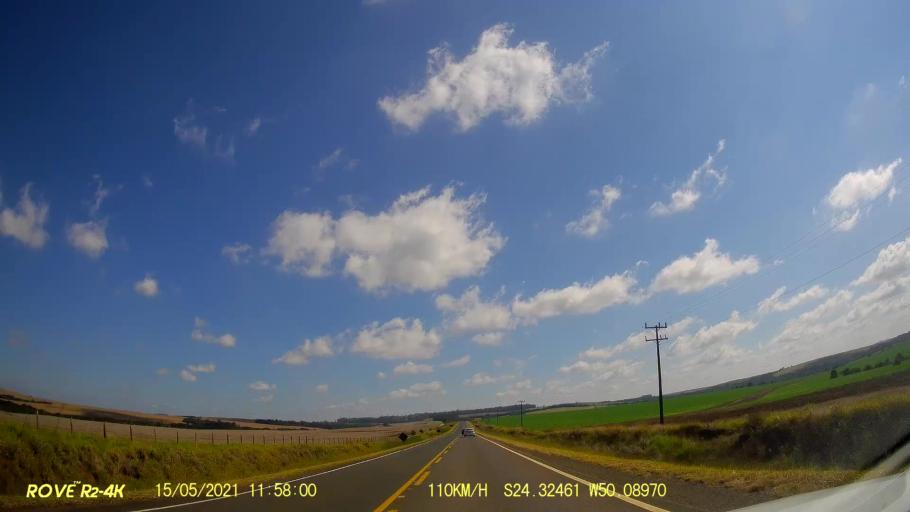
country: BR
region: Parana
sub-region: Pirai Do Sul
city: Pirai do Sul
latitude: -24.3247
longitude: -50.0898
